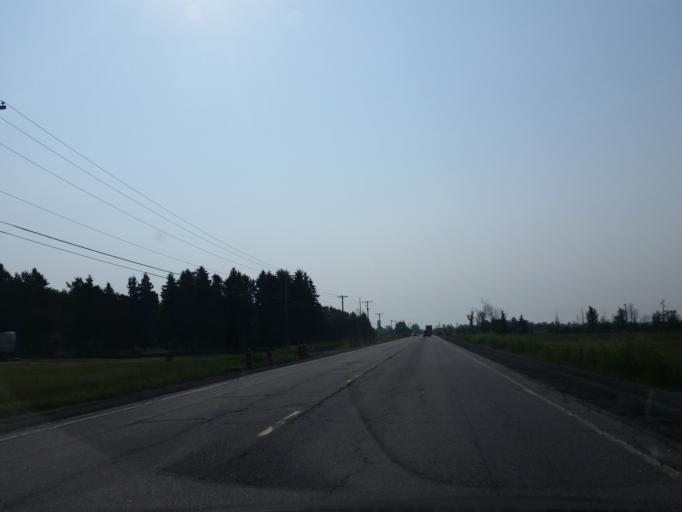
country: CA
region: Ontario
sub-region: Nipissing District
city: North Bay
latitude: 46.4176
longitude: -80.1485
